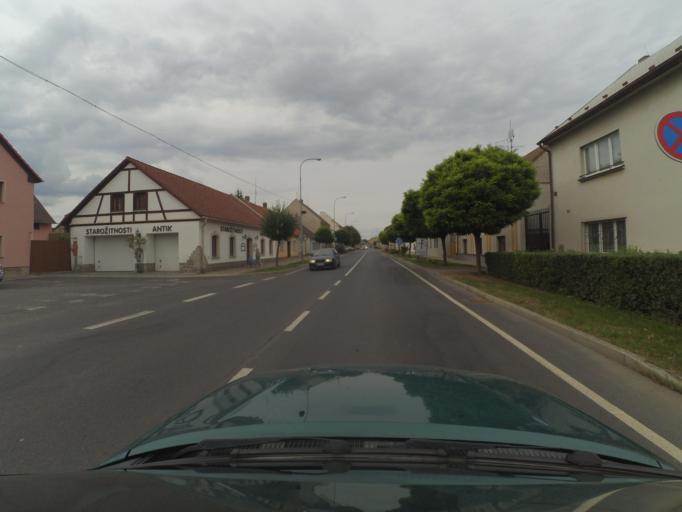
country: CZ
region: Ustecky
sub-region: Okres Louny
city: Louny
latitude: 50.3328
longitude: 13.8121
